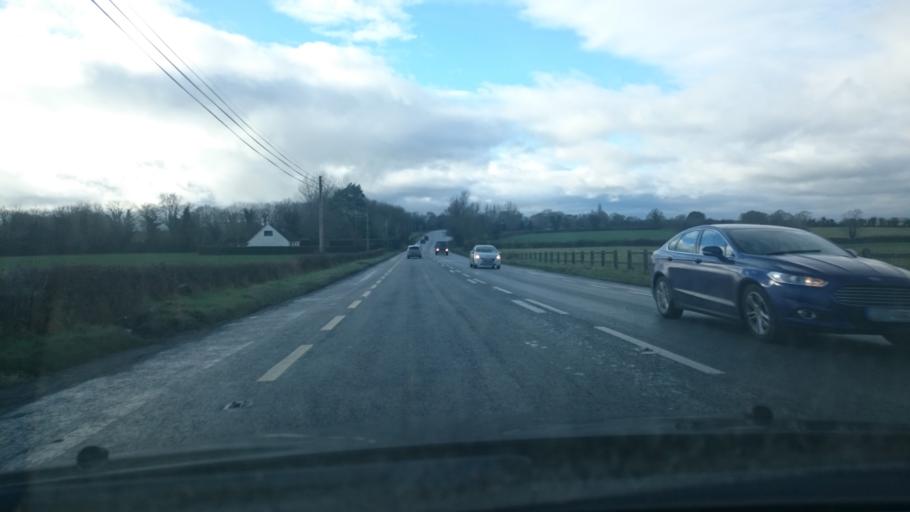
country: IE
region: Leinster
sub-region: Kilkenny
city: Callan
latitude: 52.5606
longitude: -7.3661
